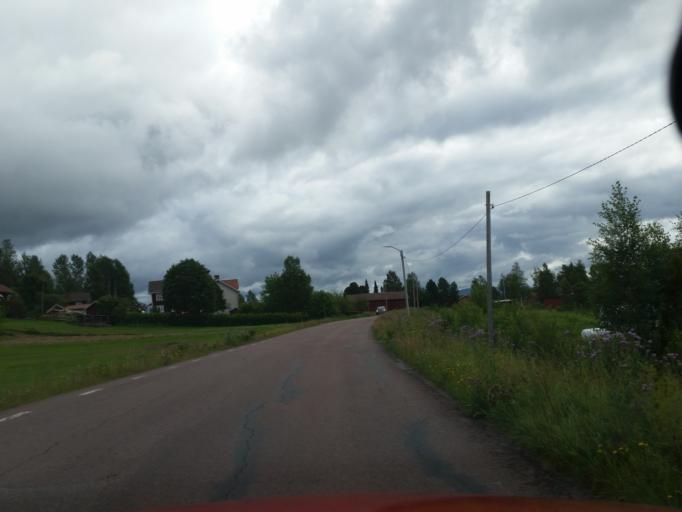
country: SE
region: Dalarna
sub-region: Leksand Municipality
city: Smedby
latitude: 60.7172
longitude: 15.0438
